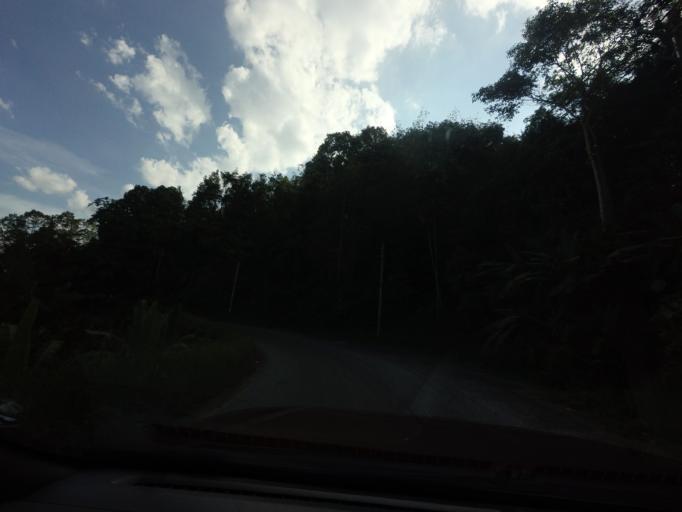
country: TH
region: Yala
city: Than To
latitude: 6.1408
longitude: 101.2961
